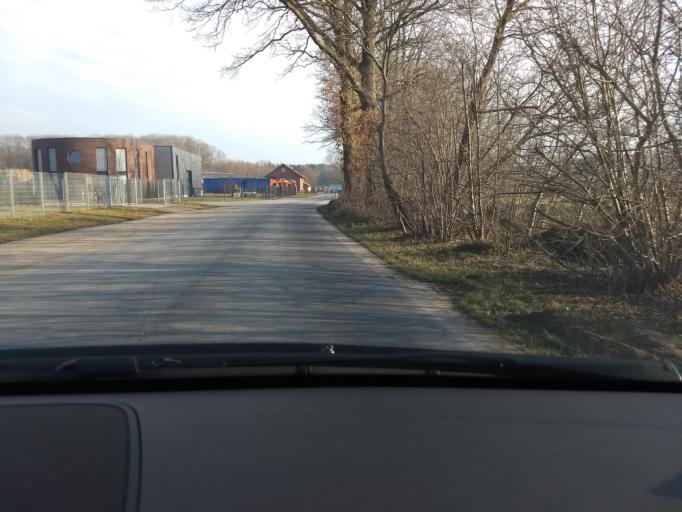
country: DE
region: North Rhine-Westphalia
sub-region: Regierungsbezirk Munster
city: Rhede
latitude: 51.8333
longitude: 6.7202
